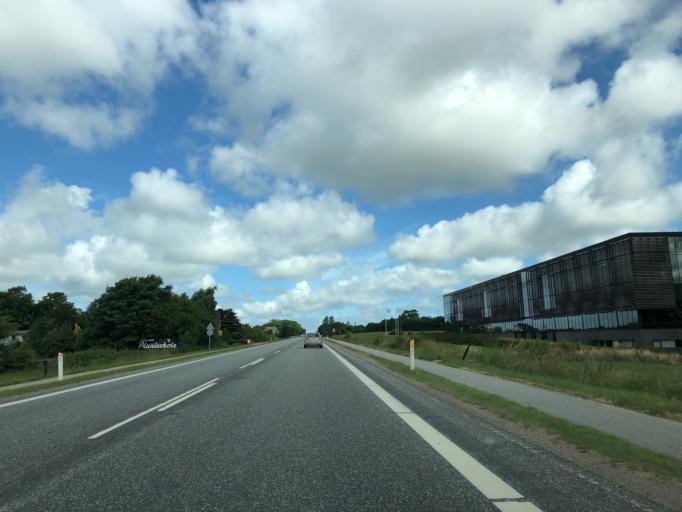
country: DK
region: Central Jutland
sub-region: Holstebro Kommune
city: Holstebro
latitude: 56.3905
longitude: 8.6106
